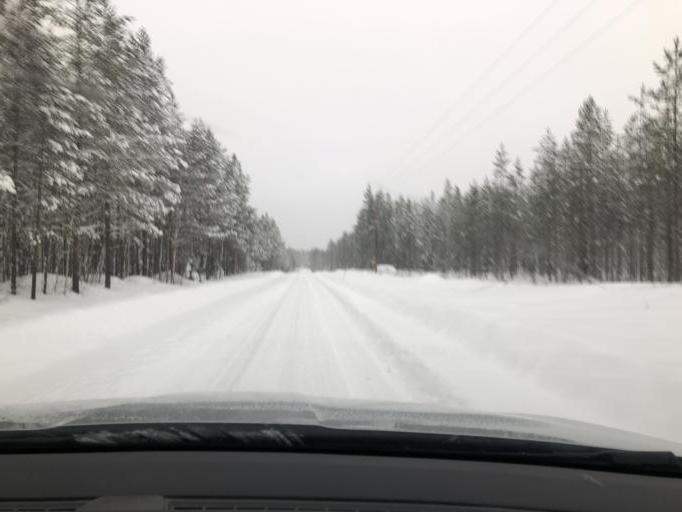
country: SE
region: Vaesterbotten
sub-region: Umea Kommun
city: Saevar
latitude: 63.9460
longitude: 20.7003
